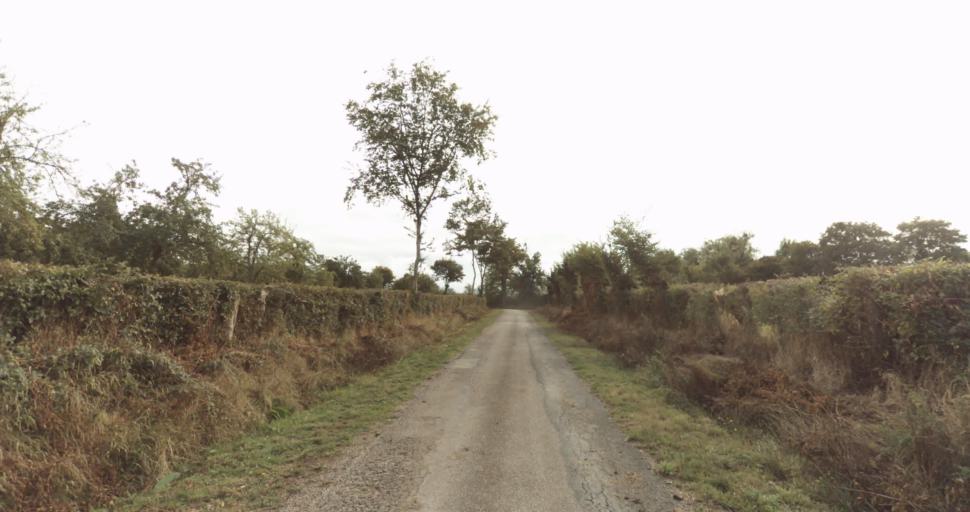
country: FR
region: Lower Normandy
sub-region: Departement de l'Orne
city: Vimoutiers
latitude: 48.8684
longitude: 0.1631
